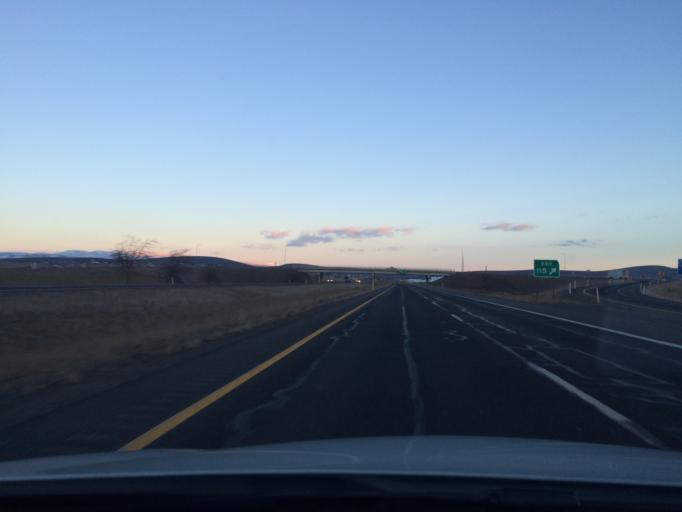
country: US
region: Washington
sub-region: Kittitas County
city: Kittitas
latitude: 46.9714
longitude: -120.4176
